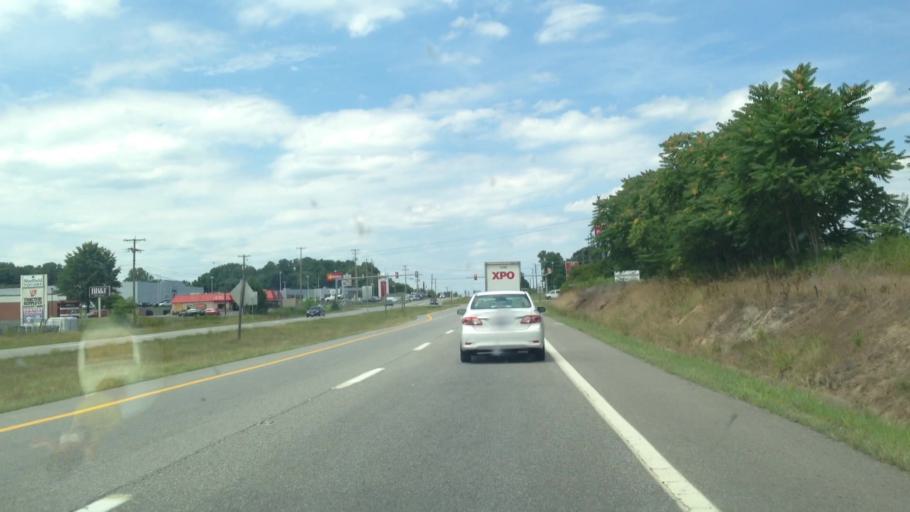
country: US
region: Virginia
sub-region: Henry County
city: Chatmoss
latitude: 36.6257
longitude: -79.8596
